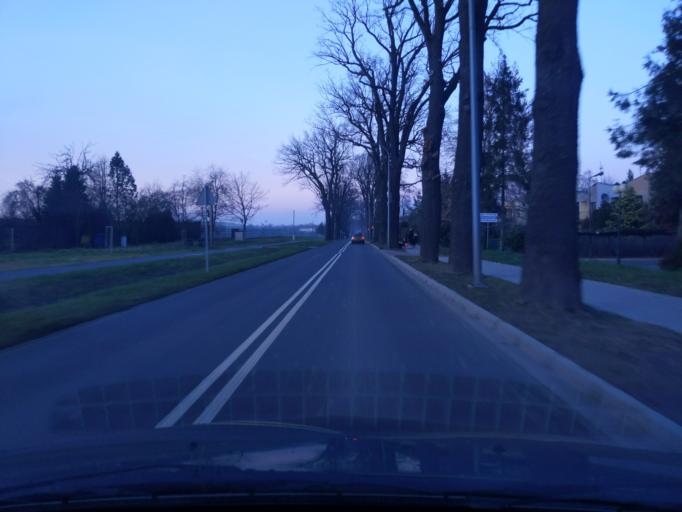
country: PL
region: Silesian Voivodeship
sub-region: Powiat pszczynski
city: Pszczyna
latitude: 49.9615
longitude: 18.9331
